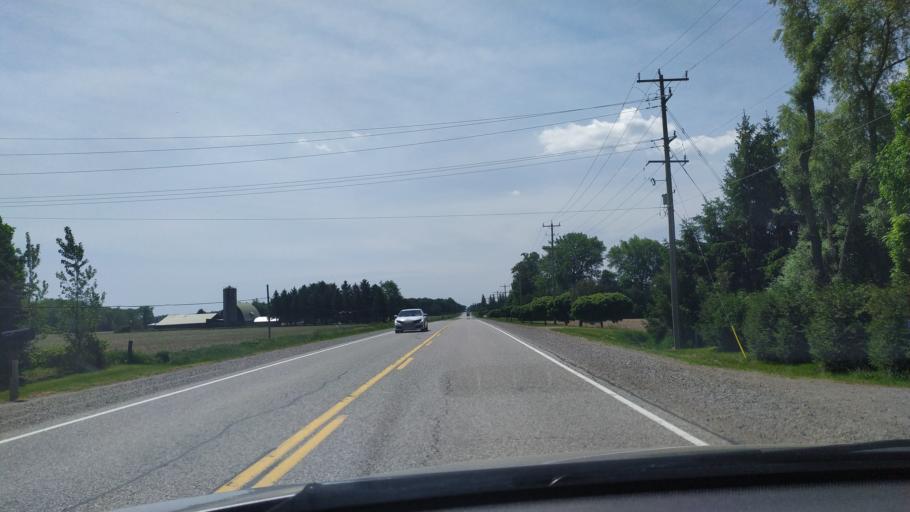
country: CA
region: Ontario
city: Dorchester
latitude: 43.1079
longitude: -81.0143
